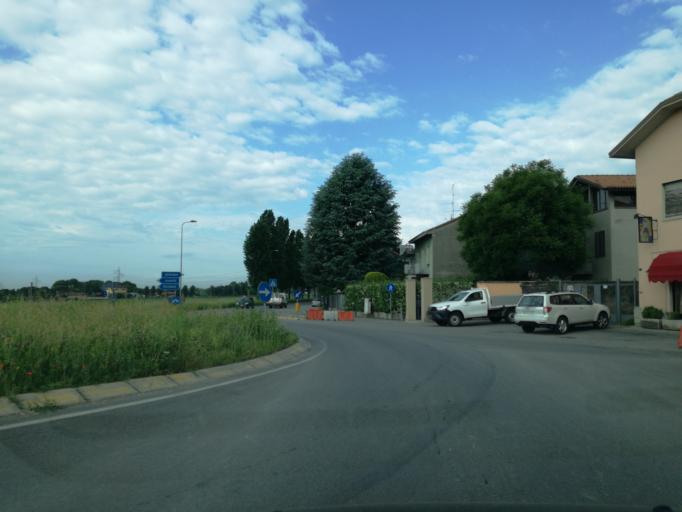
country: IT
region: Lombardy
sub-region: Provincia di Monza e Brianza
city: Albiate
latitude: 45.6508
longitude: 9.2396
